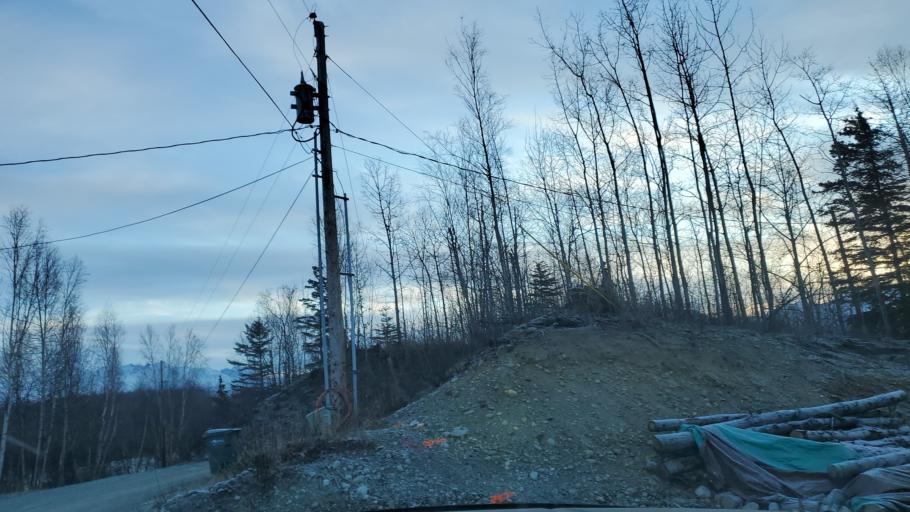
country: US
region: Alaska
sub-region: Matanuska-Susitna Borough
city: Lakes
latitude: 61.6022
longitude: -149.3119
